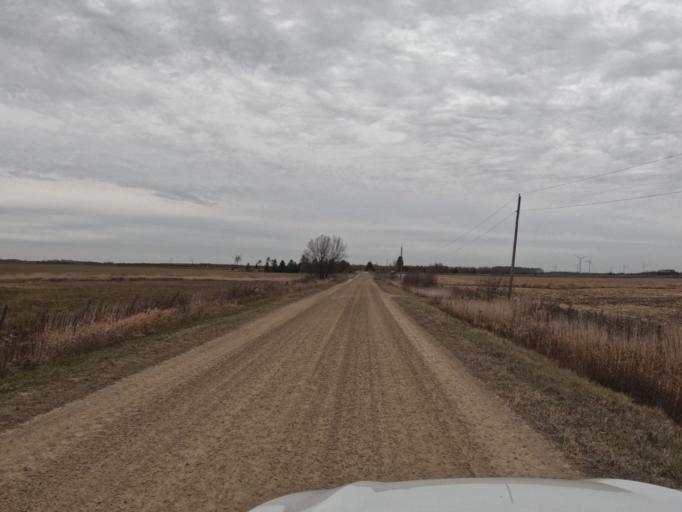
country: CA
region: Ontario
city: Shelburne
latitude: 44.0358
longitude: -80.3724
